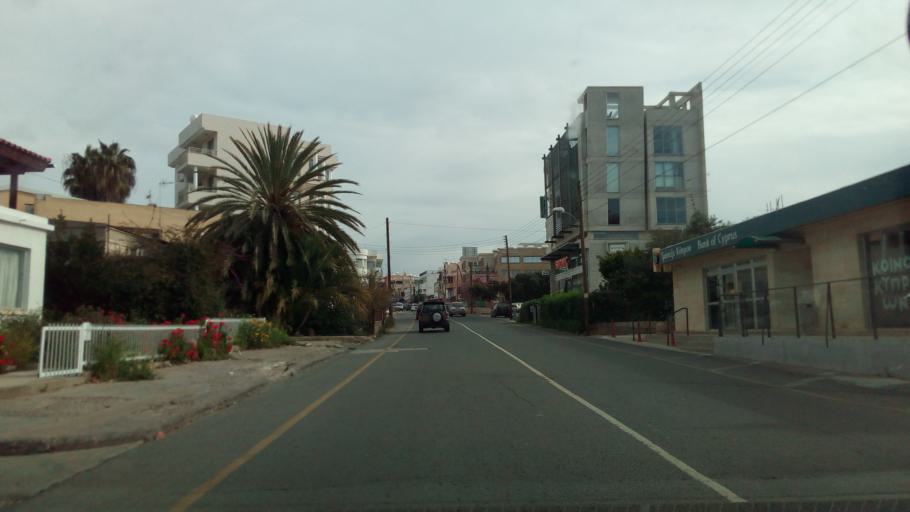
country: CY
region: Pafos
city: Paphos
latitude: 34.7842
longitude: 32.4303
